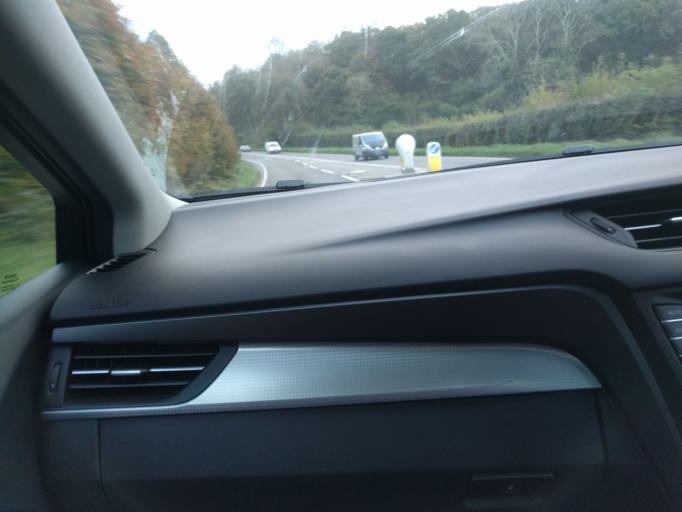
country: GB
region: England
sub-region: Cornwall
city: Perranarworthal
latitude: 50.1996
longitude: -5.1241
